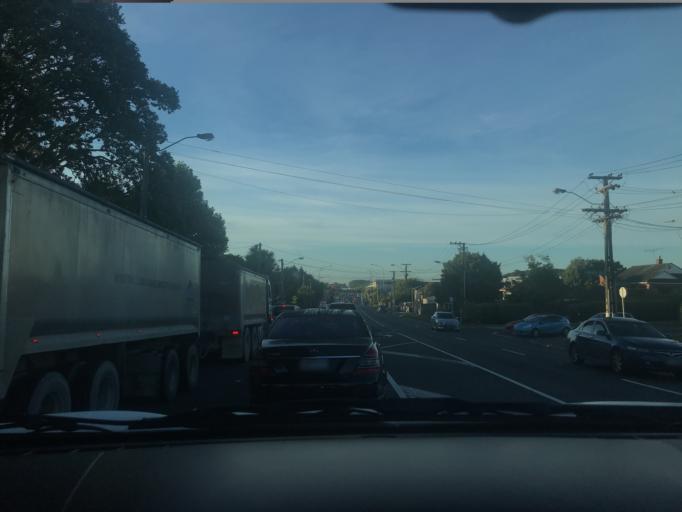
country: NZ
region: Auckland
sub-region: Auckland
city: Tamaki
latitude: -36.9114
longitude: 174.8380
